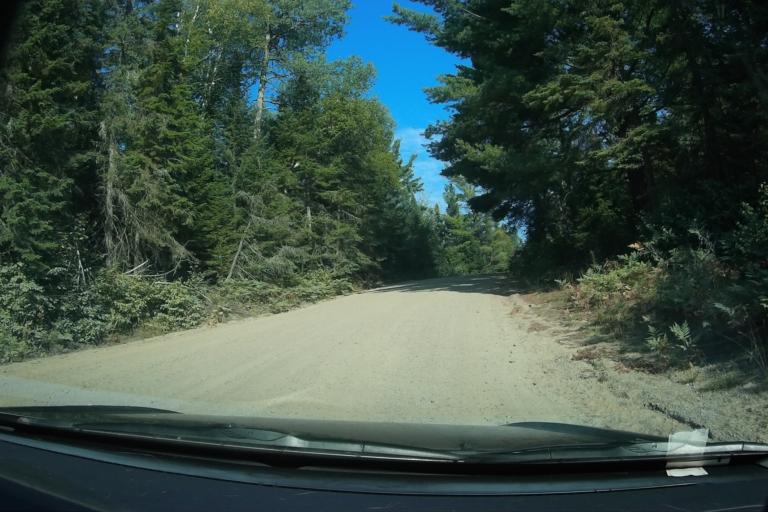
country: CA
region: Ontario
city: Huntsville
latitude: 45.5678
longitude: -78.7094
